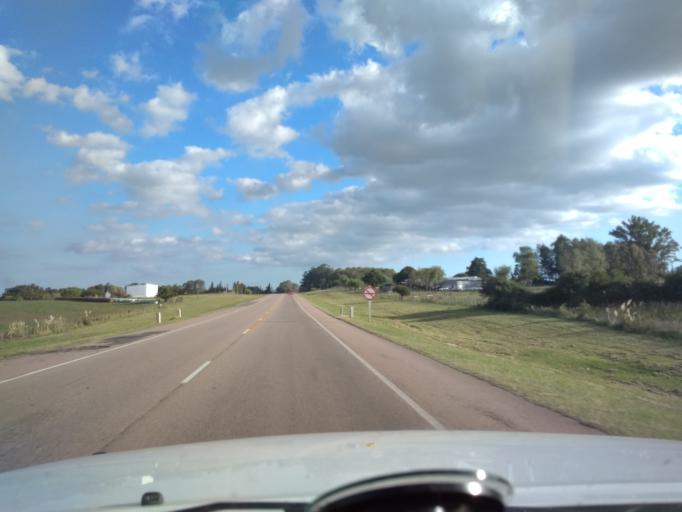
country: UY
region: Canelones
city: Canelones
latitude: -34.4483
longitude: -56.2660
